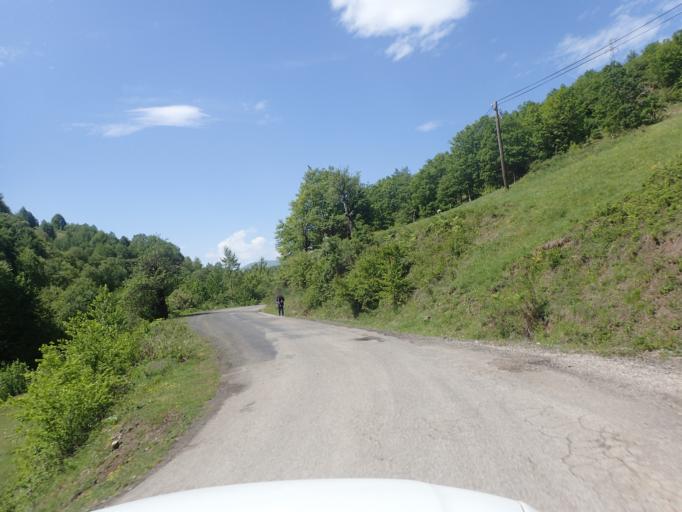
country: TR
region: Ordu
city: Akkus
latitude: 40.8026
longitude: 36.9487
